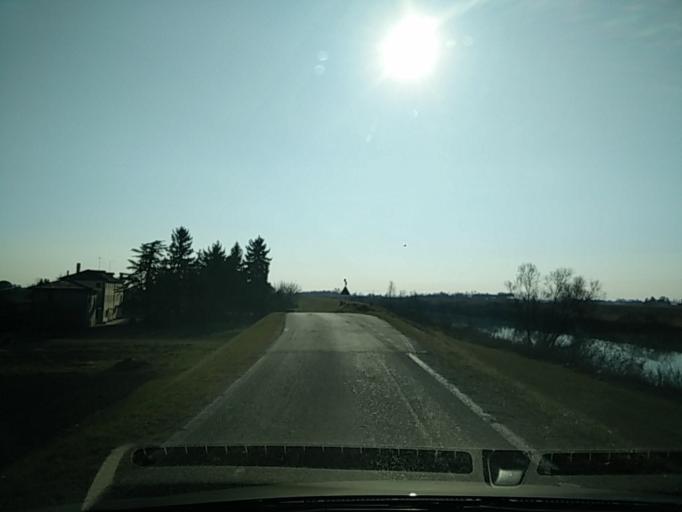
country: IT
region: Veneto
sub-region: Provincia di Venezia
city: Torre di Mosto
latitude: 45.6879
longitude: 12.7251
